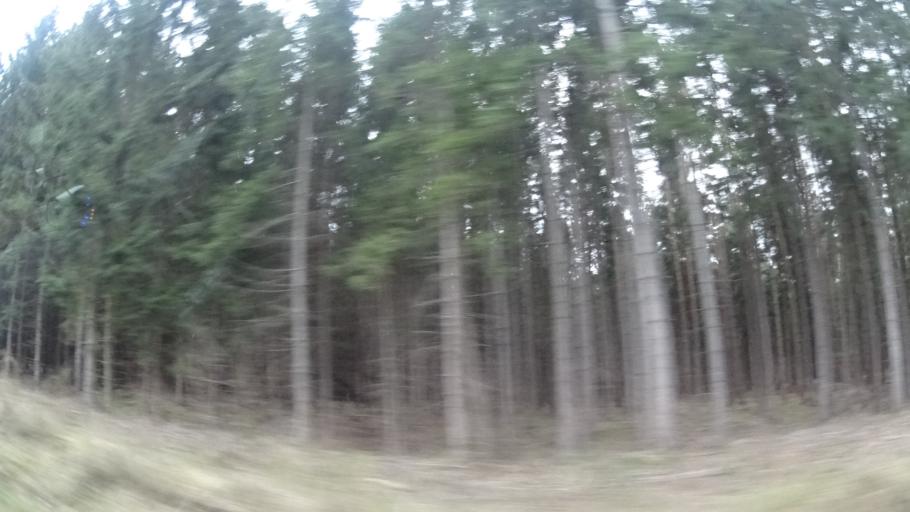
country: DE
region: Thuringia
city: Auma
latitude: 50.7084
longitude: 11.8874
